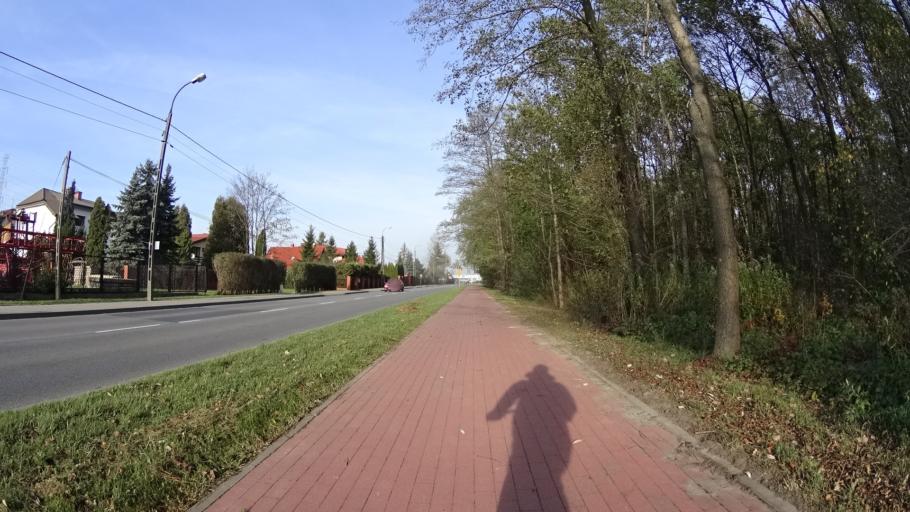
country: PL
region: Masovian Voivodeship
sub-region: Powiat warszawski zachodni
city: Babice
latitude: 52.2729
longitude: 20.8638
